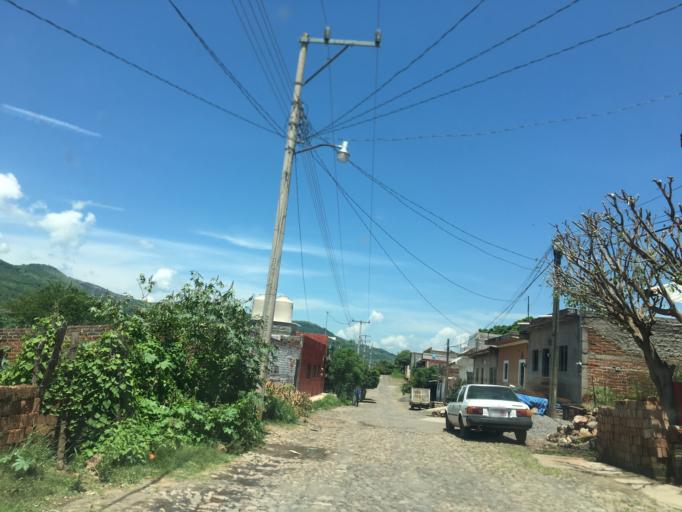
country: MX
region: Nayarit
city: Ixtlan del Rio
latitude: 21.0384
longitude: -104.3546
